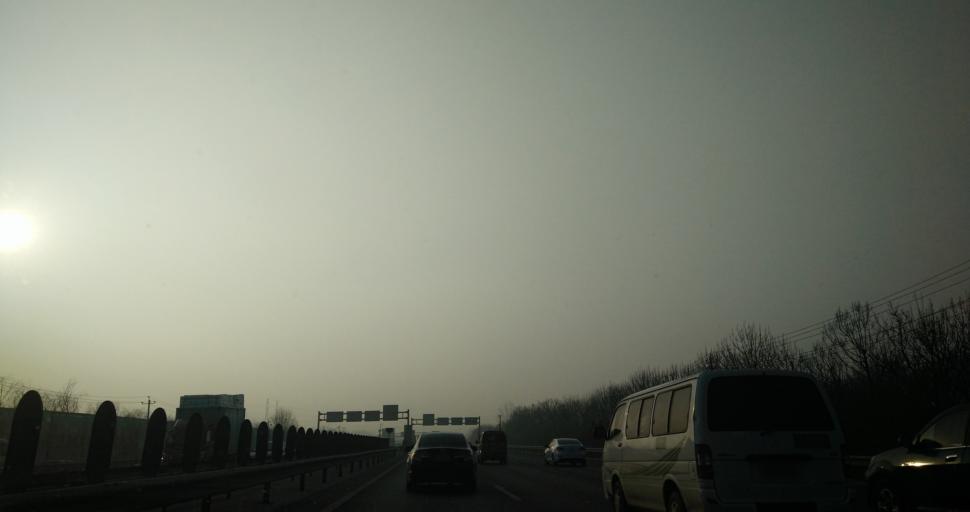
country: CN
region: Beijing
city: Nanyuan
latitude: 39.7584
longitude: 116.3848
